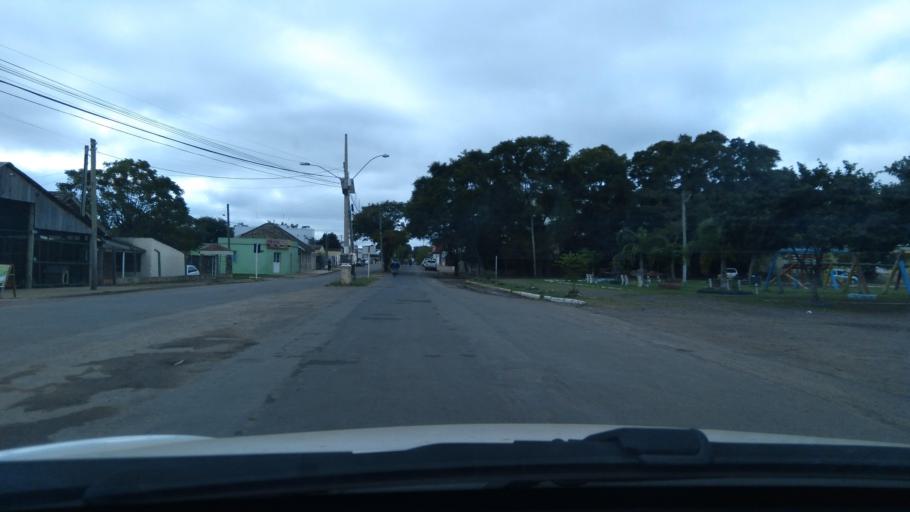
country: BR
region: Rio Grande do Sul
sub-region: Dom Pedrito
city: Dom Pedrito
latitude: -30.9737
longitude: -54.6740
